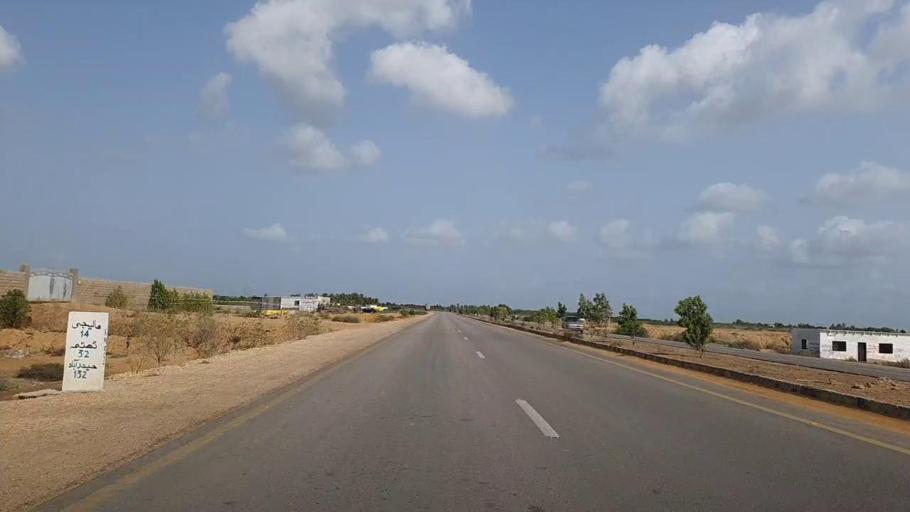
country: PK
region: Sindh
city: Gharo
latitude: 24.7338
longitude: 67.6017
